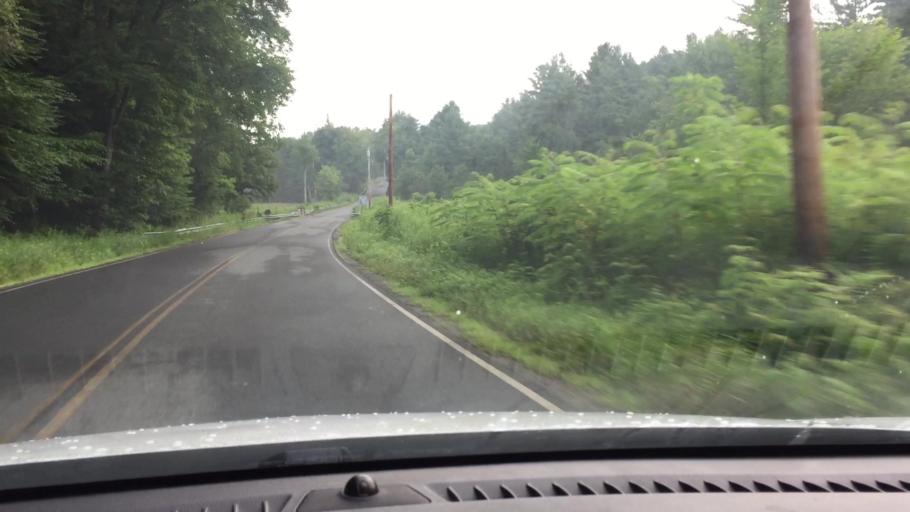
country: US
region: Massachusetts
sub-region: Hampshire County
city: Westhampton
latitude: 42.2620
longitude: -72.9096
